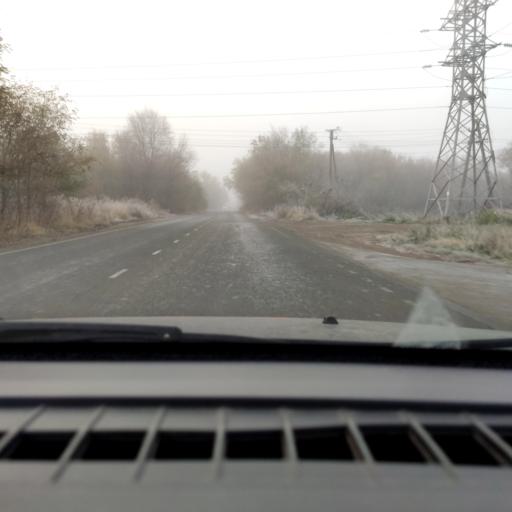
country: RU
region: Samara
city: Tol'yatti
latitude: 53.5833
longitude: 49.2567
